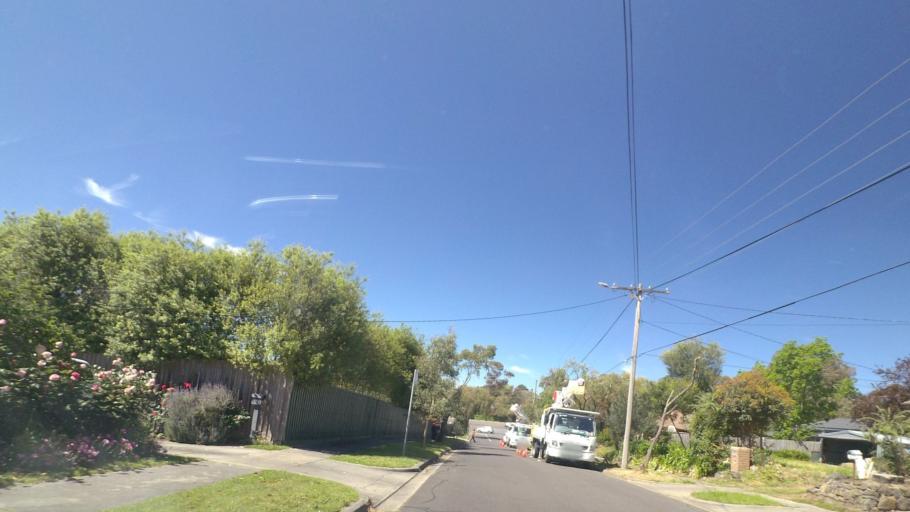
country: AU
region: Victoria
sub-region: Maroondah
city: Heathmont
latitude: -37.8264
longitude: 145.2604
